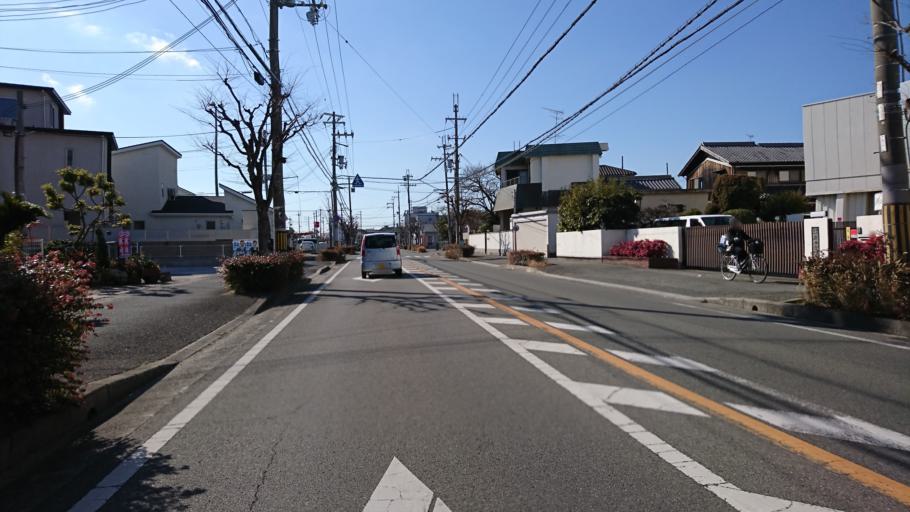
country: JP
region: Hyogo
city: Kakogawacho-honmachi
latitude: 34.7772
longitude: 134.8052
